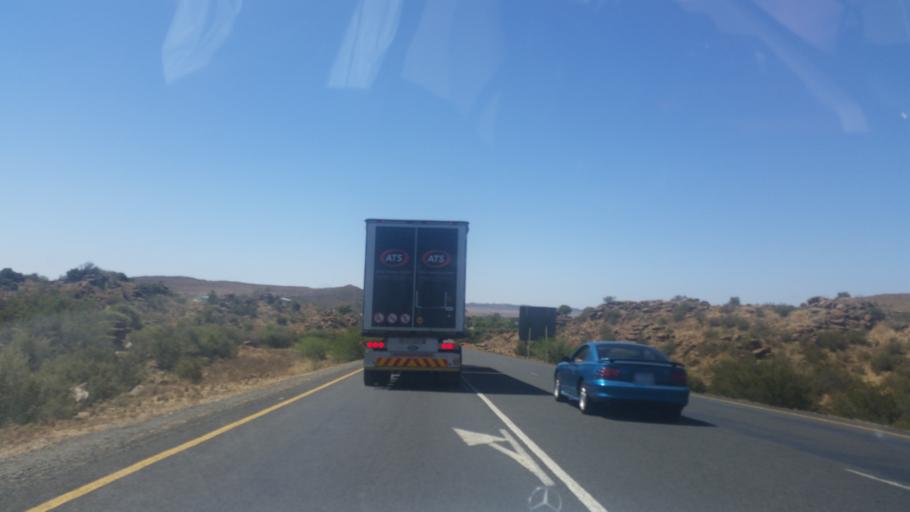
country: ZA
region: Northern Cape
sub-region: Pixley ka Seme District Municipality
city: Colesberg
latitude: -30.7167
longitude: 25.0958
